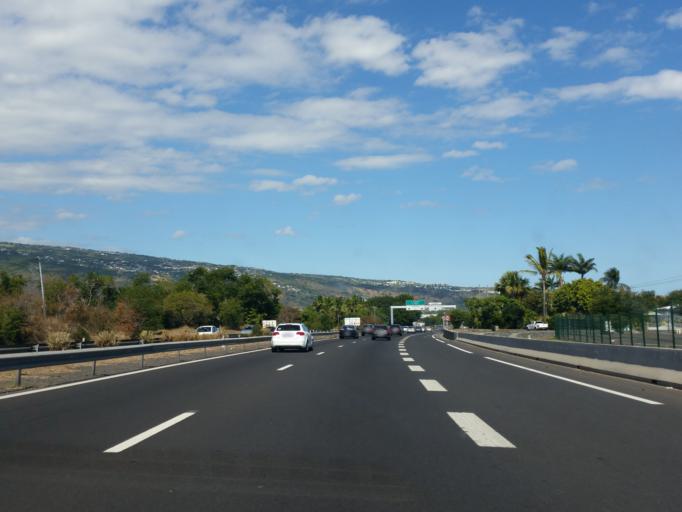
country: RE
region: Reunion
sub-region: Reunion
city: Le Port
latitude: -20.9745
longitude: 55.2980
